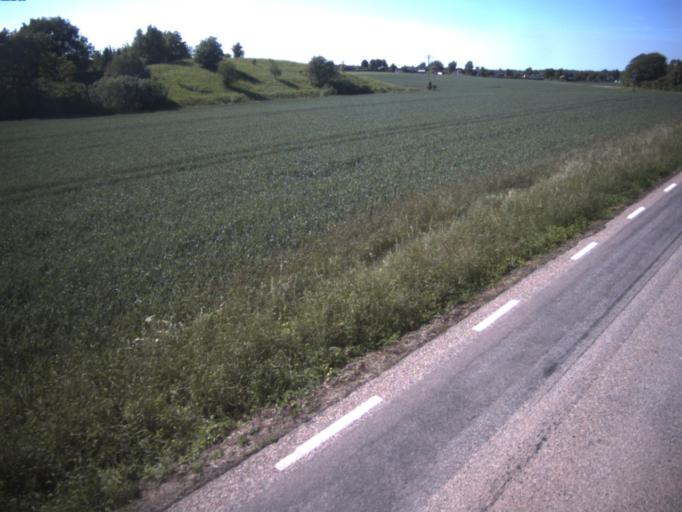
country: SE
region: Skane
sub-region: Helsingborg
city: Gantofta
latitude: 55.9806
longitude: 12.8125
